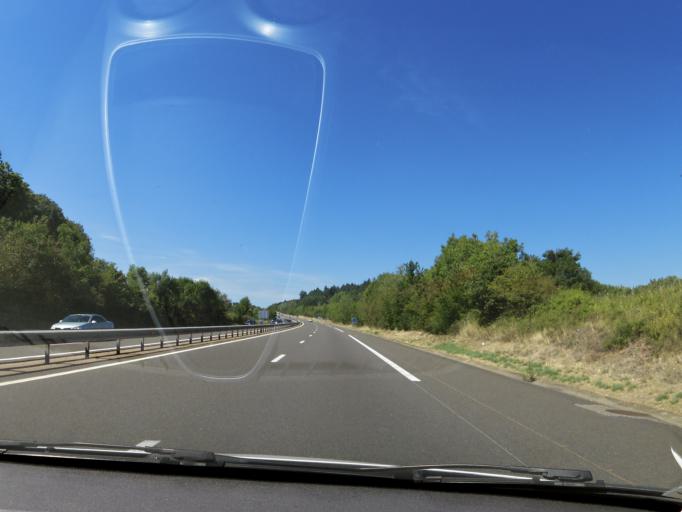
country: FR
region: Rhone-Alpes
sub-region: Departement de la Loire
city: Saint-Germain-Laval
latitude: 45.8697
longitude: 3.9480
